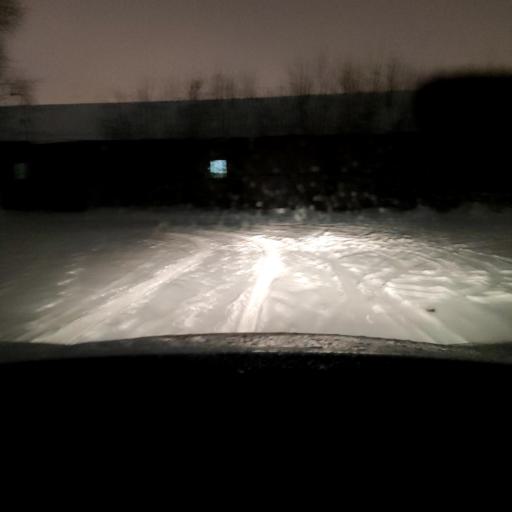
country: RU
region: Tatarstan
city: Verkhniy Uslon
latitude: 55.8102
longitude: 49.0476
